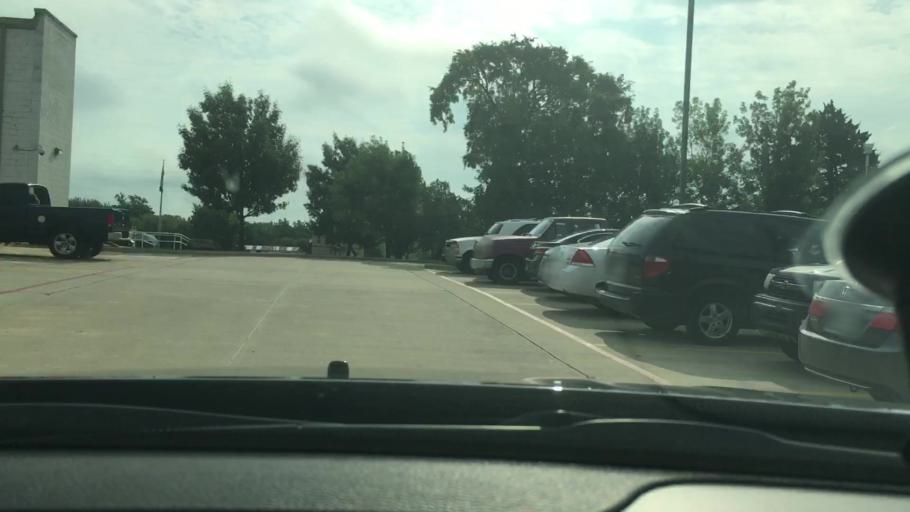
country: US
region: Oklahoma
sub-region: Carter County
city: Ardmore
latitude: 34.1605
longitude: -97.1453
